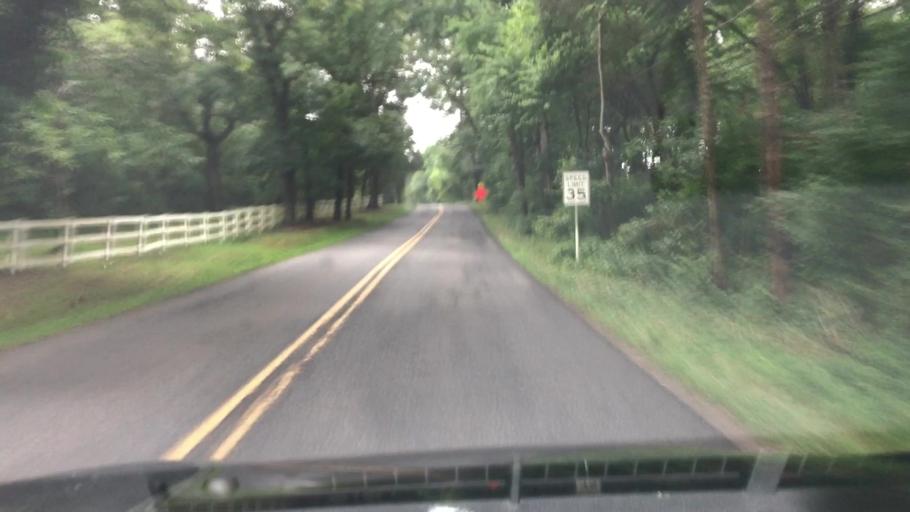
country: US
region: Virginia
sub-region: Prince William County
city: Nokesville
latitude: 38.6644
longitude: -77.6460
